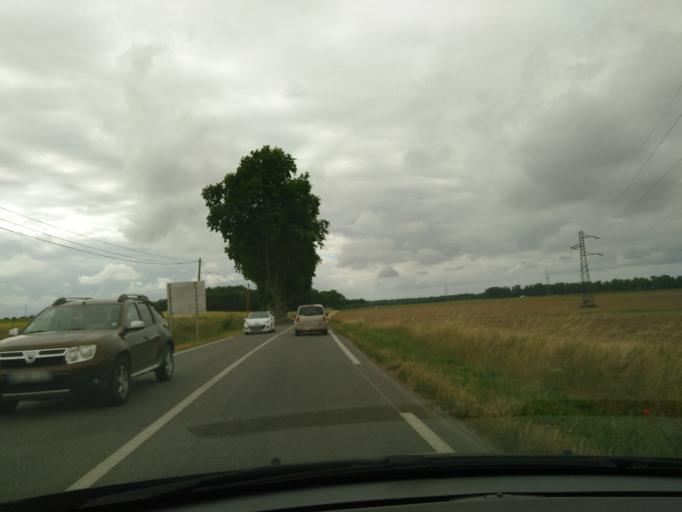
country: FR
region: Midi-Pyrenees
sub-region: Departement de la Haute-Garonne
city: Grenade
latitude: 43.7838
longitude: 1.2734
